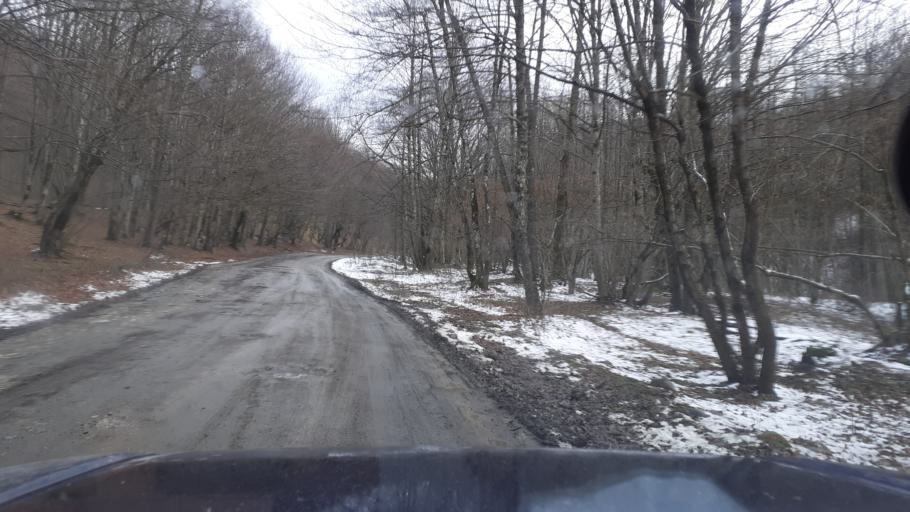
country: RU
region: Krasnodarskiy
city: Neftegorsk
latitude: 44.0708
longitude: 39.7095
